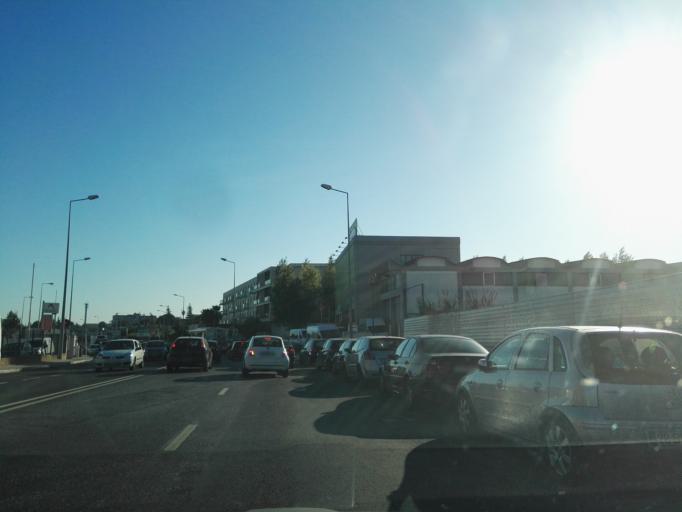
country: PT
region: Lisbon
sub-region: Loures
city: Sacavem
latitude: 38.7846
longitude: -9.1246
